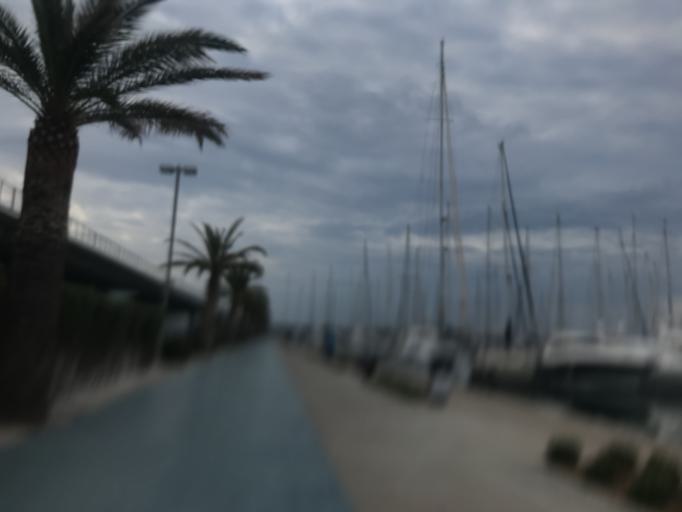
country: ES
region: Valencia
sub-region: Provincia de Valencia
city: Alboraya
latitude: 39.4626
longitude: -0.3161
